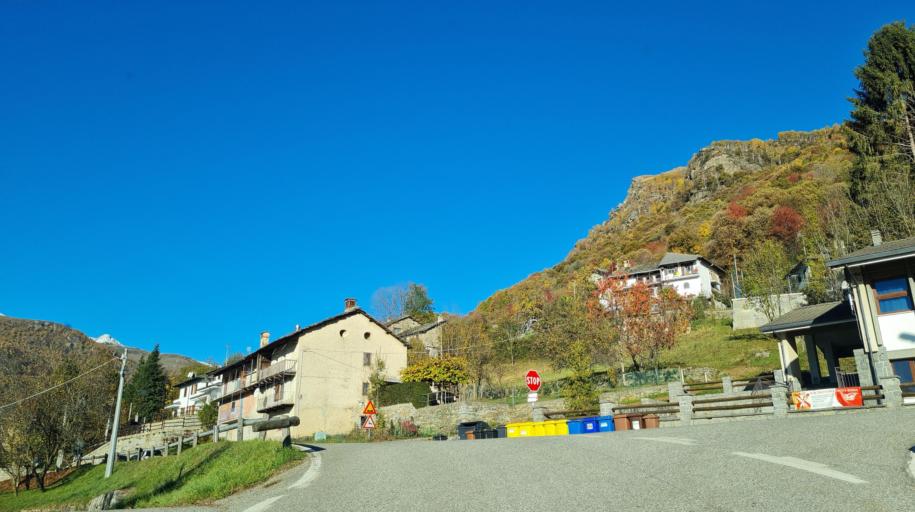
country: IT
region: Piedmont
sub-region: Provincia di Torino
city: Traversella
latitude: 45.5083
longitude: 7.7468
